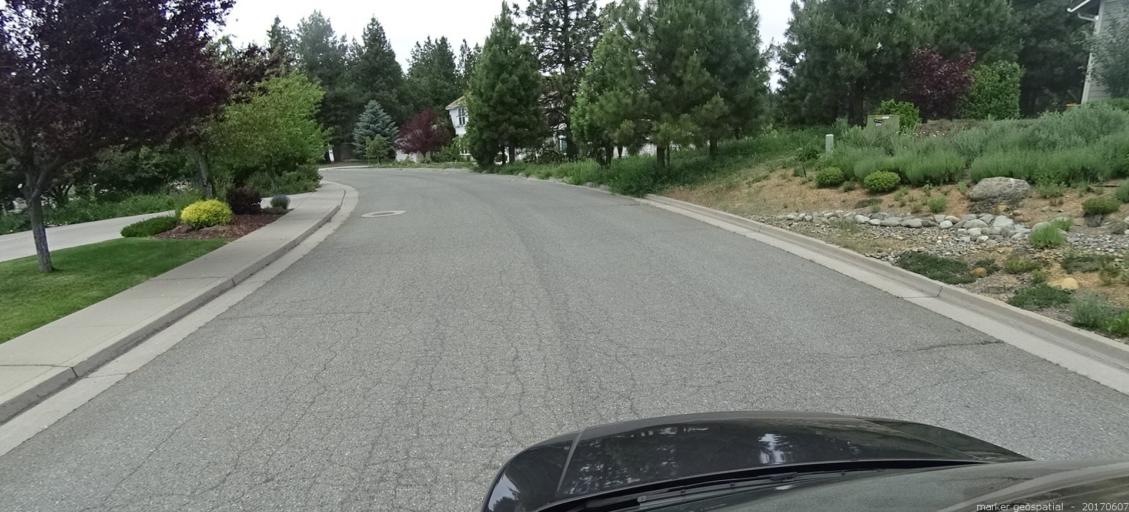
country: US
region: California
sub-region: Siskiyou County
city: Mount Shasta
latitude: 41.2932
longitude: -122.3147
